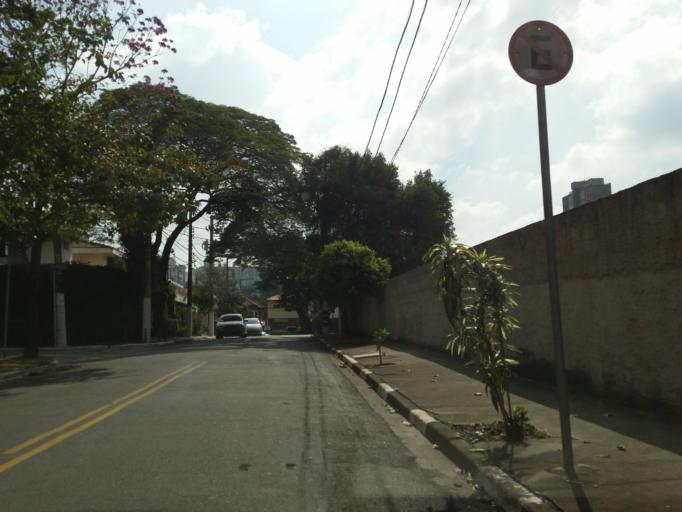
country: BR
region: Sao Paulo
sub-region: Diadema
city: Diadema
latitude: -23.6537
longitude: -46.6944
